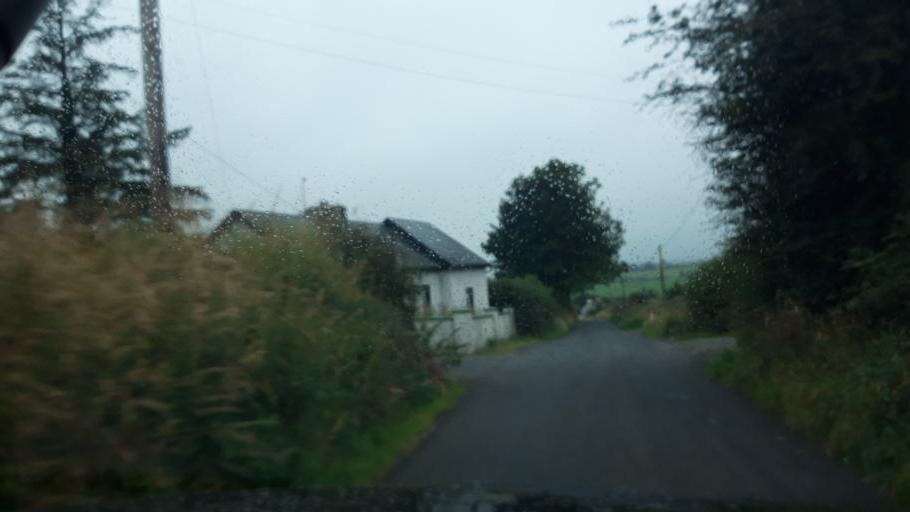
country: IE
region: Leinster
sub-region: Kilkenny
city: Callan
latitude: 52.6311
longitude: -7.5468
